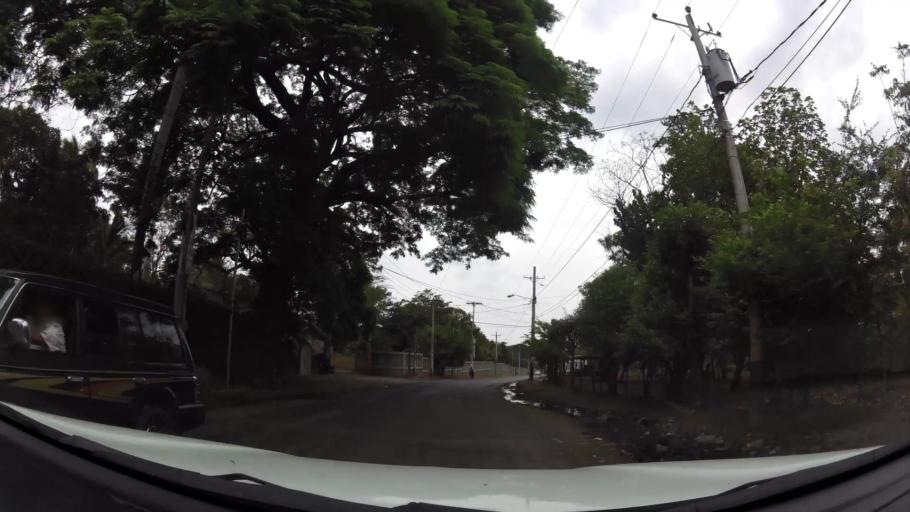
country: NI
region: Masaya
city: Ticuantepe
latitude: 12.0609
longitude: -86.1932
